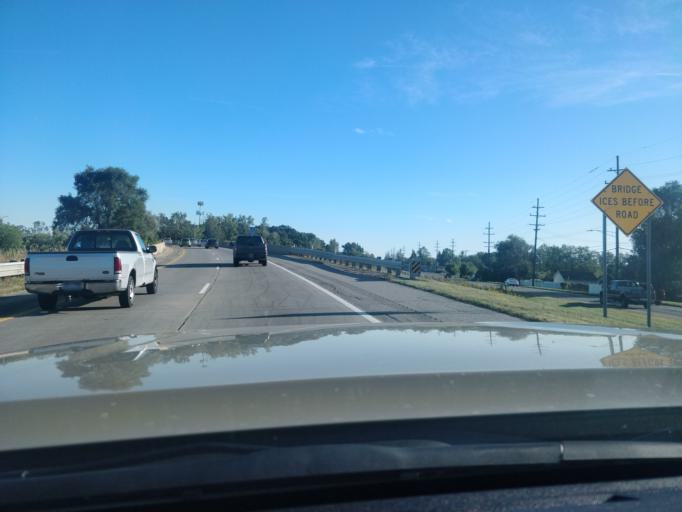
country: US
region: Michigan
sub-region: Wayne County
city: Taylor
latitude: 42.1940
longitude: -83.2678
